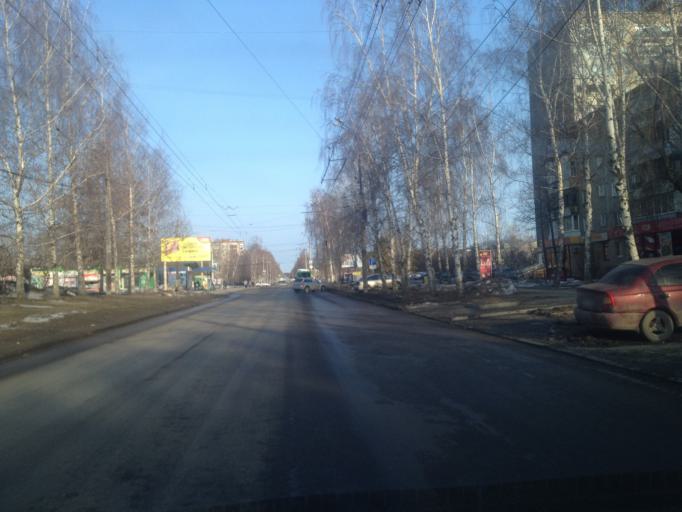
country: RU
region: Sverdlovsk
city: Sovkhoznyy
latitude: 56.8013
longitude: 60.5697
